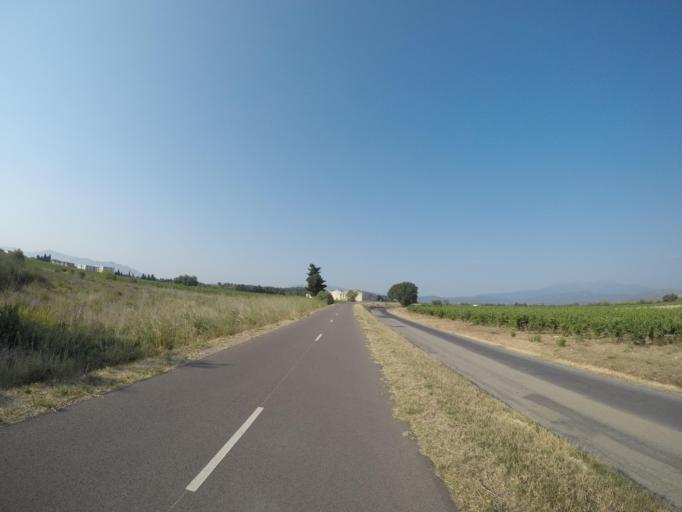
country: FR
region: Languedoc-Roussillon
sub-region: Departement des Pyrenees-Orientales
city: Ponteilla
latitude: 42.6311
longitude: 2.8061
